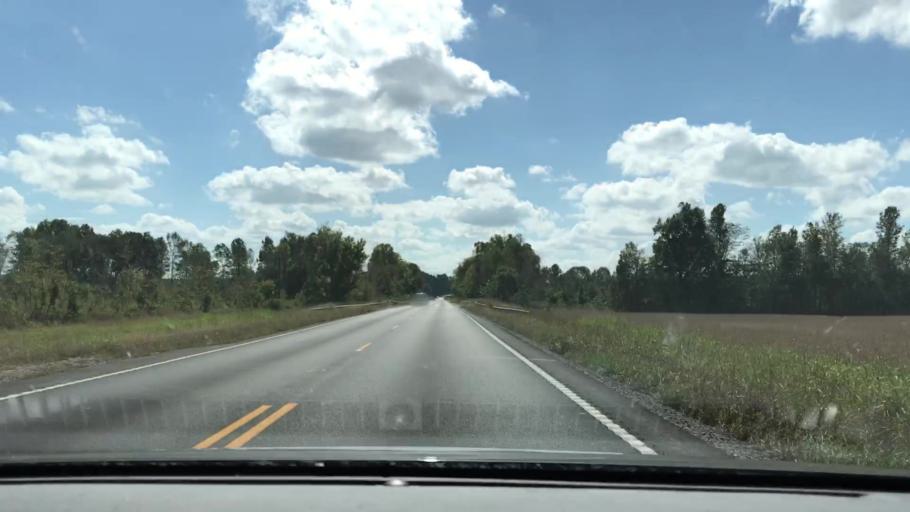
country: US
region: Kentucky
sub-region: Graves County
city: Mayfield
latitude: 36.8649
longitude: -88.5732
